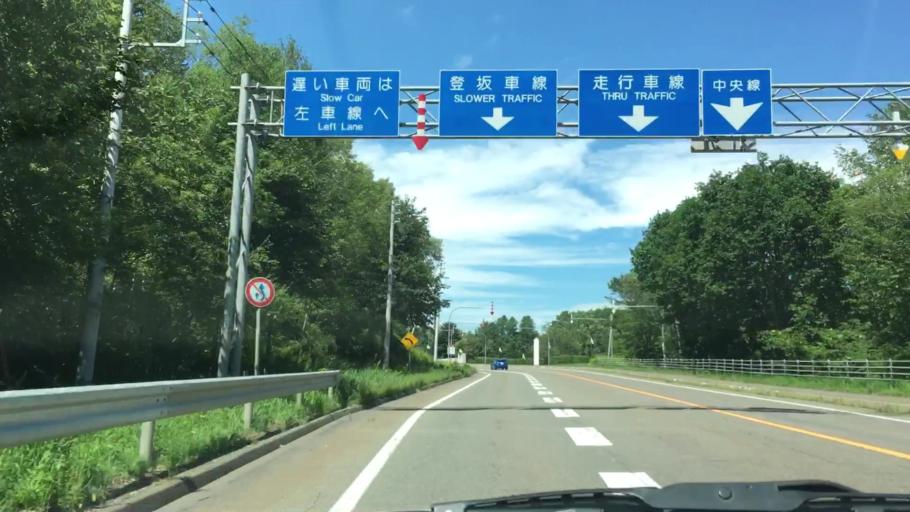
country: JP
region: Hokkaido
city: Otofuke
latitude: 43.2367
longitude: 143.5387
